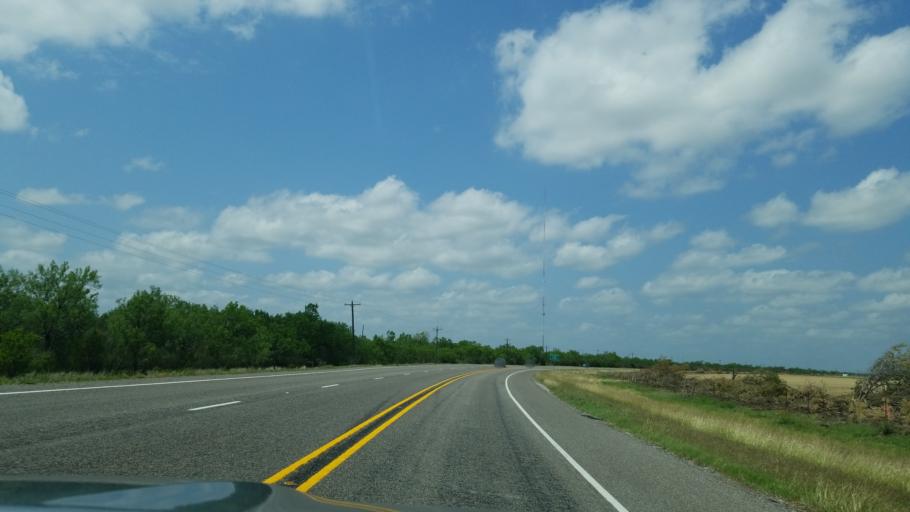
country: US
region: Texas
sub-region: Frio County
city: Pearsall
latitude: 28.9481
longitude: -99.2704
